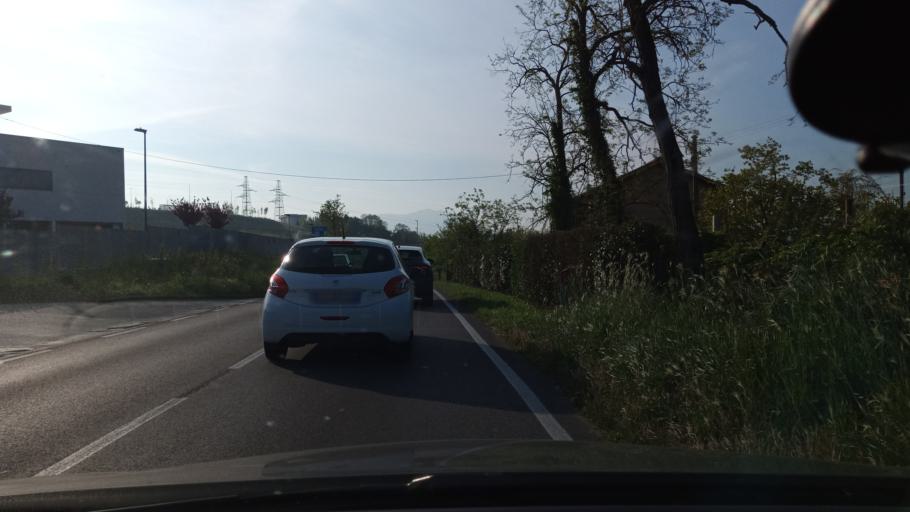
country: IT
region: Latium
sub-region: Citta metropolitana di Roma Capitale
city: Fiano Romano
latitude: 42.1676
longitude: 12.6397
